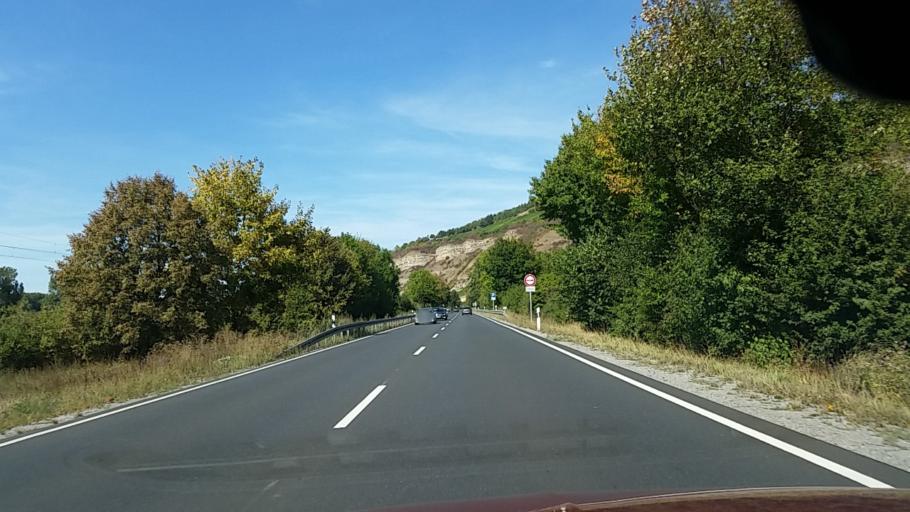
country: DE
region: Bavaria
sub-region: Regierungsbezirk Unterfranken
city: Thungersheim
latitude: 49.8886
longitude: 9.8365
